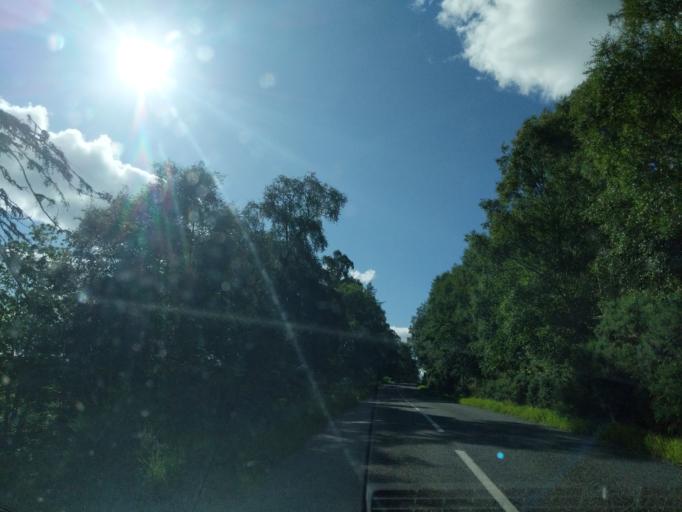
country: GB
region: Scotland
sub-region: Aberdeenshire
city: Torphins
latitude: 57.0329
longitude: -2.6602
